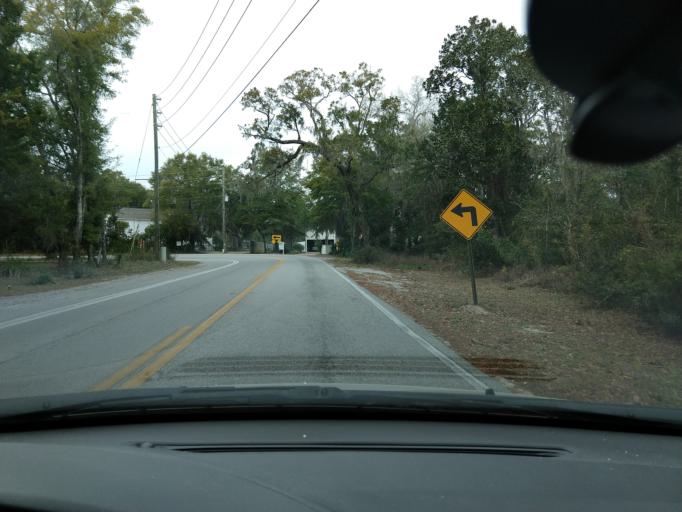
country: US
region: Florida
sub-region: Walton County
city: Miramar Beach
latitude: 30.3989
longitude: -86.3042
